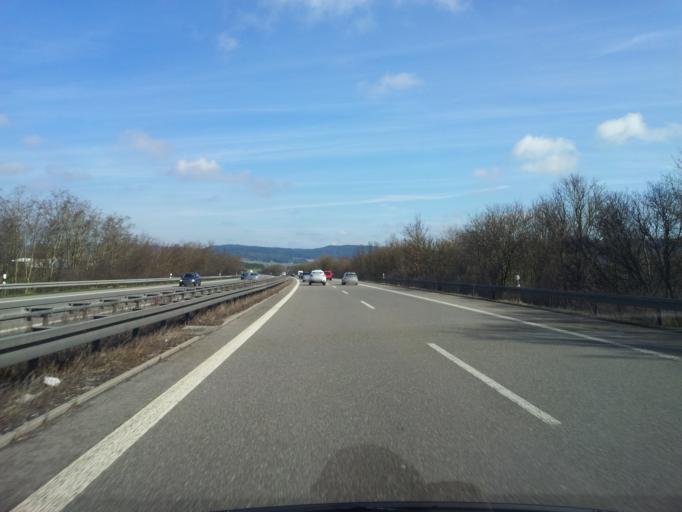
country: DE
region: Baden-Wuerttemberg
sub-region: Freiburg Region
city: Dietingen
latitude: 48.2237
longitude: 8.6480
